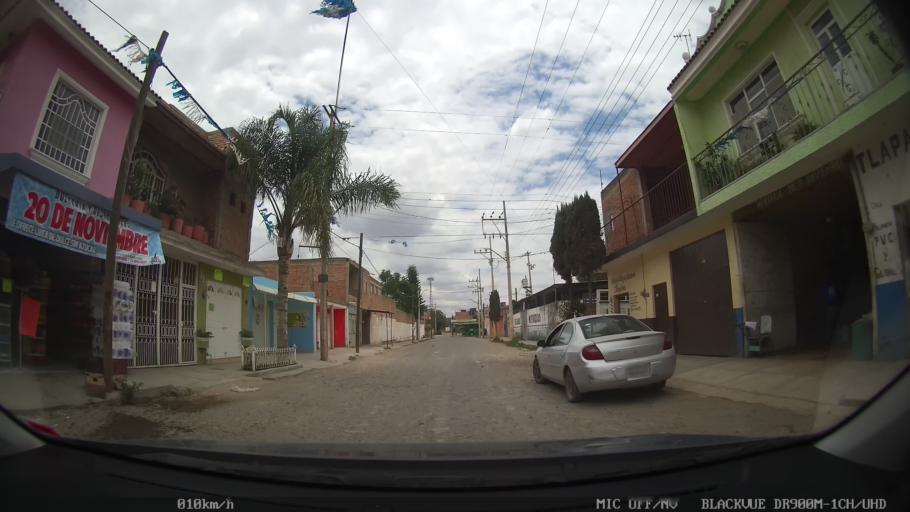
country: MX
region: Jalisco
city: Tlaquepaque
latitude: 20.6491
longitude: -103.2650
